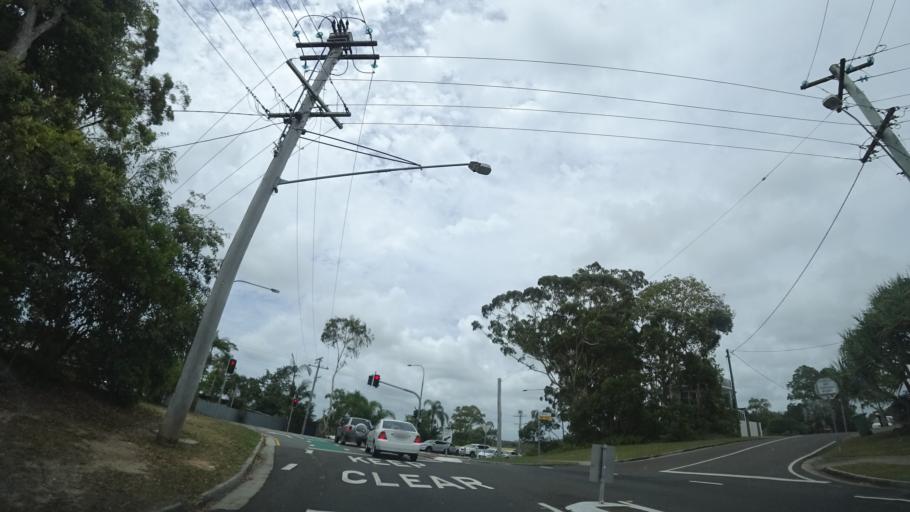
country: AU
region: Queensland
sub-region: Sunshine Coast
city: Mooloolaba
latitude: -26.6733
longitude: 153.1037
